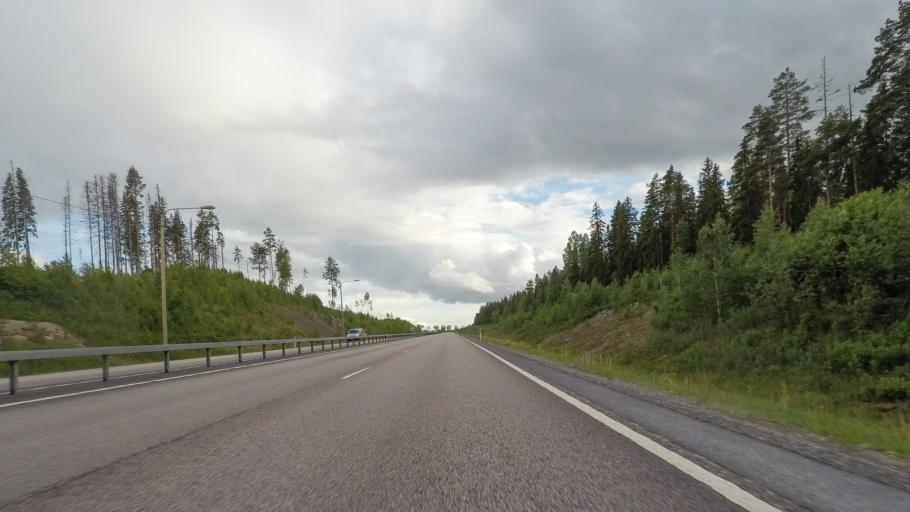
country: FI
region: Paijanne Tavastia
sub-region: Lahti
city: Heinola
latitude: 61.3673
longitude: 26.0471
